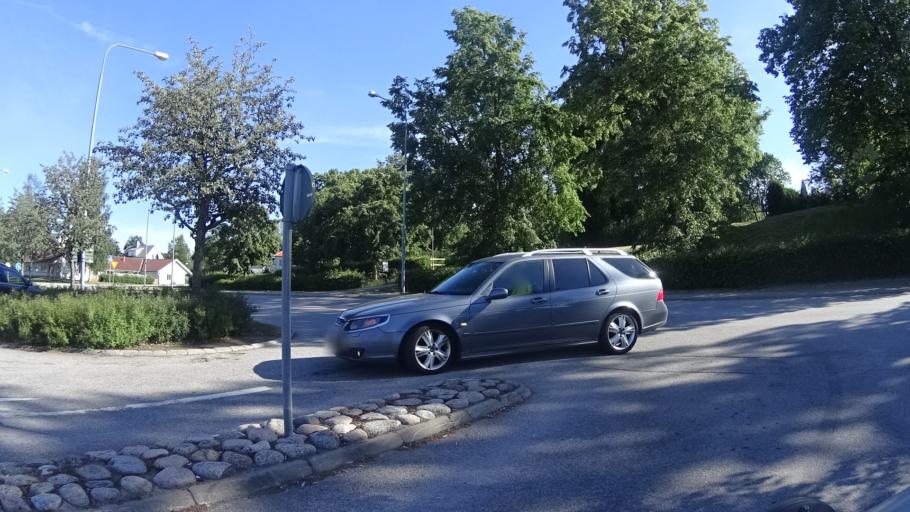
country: SE
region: Kalmar
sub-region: Vasterviks Kommun
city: Gamleby
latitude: 57.8970
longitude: 16.4003
